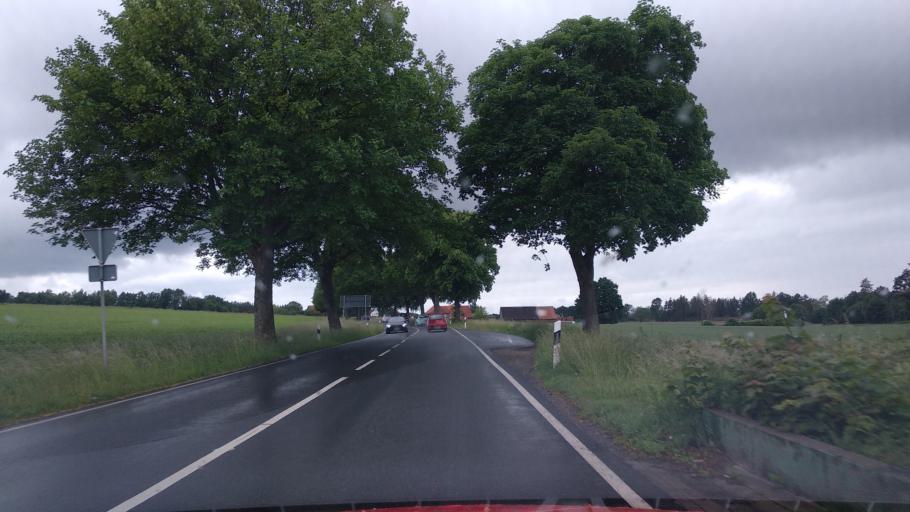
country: DE
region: Lower Saxony
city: Obernkirchen
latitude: 52.2860
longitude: 9.1424
